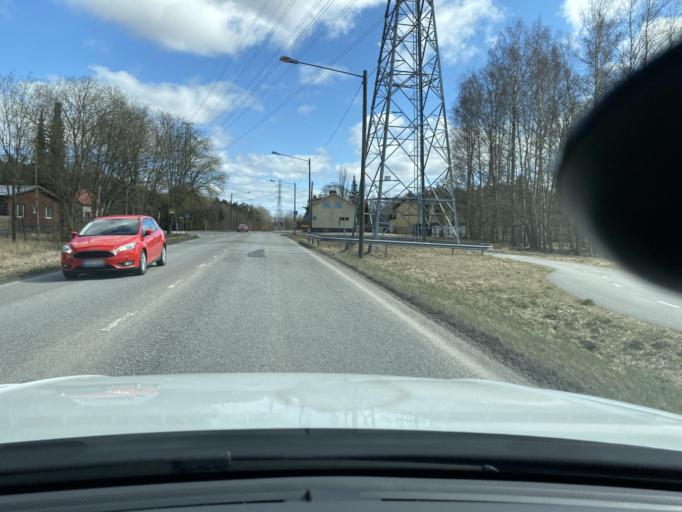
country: FI
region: Varsinais-Suomi
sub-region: Turku
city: Turku
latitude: 60.4751
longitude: 22.2716
